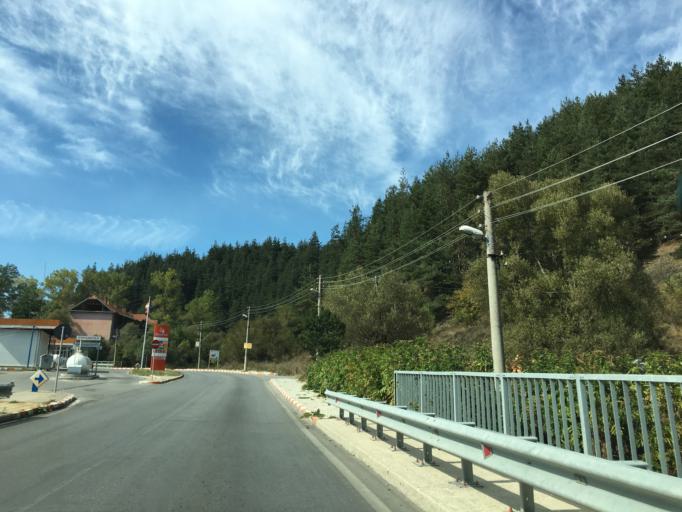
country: BG
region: Pazardzhik
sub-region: Obshtina Batak
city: Batak
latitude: 41.9477
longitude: 24.2298
